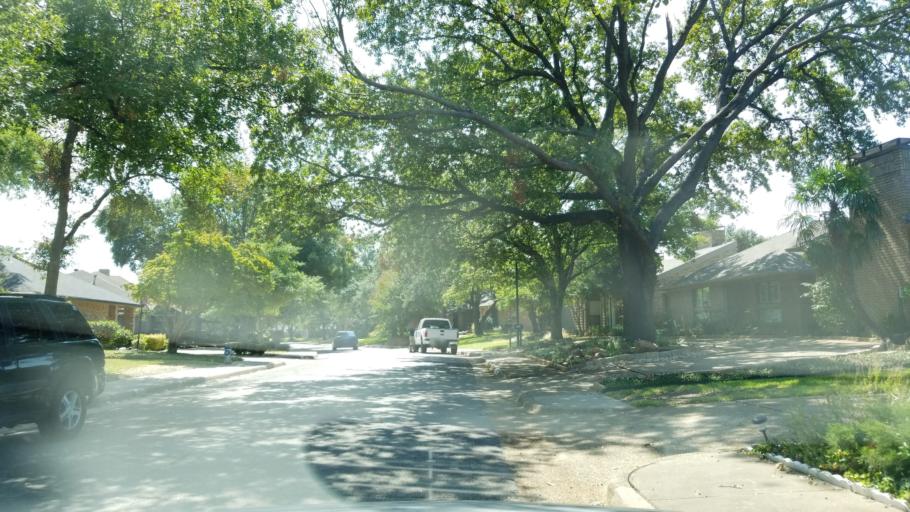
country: US
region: Texas
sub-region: Dallas County
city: Addison
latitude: 32.9662
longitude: -96.7999
